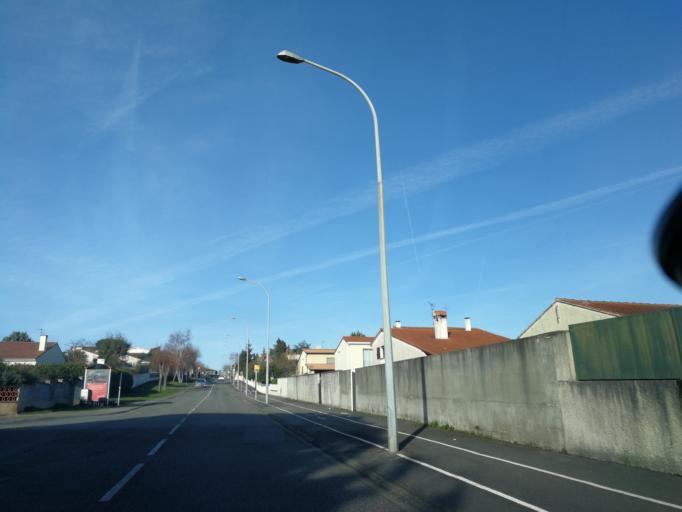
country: FR
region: Midi-Pyrenees
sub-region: Departement de la Haute-Garonne
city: Saint-Jean
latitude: 43.6491
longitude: 1.4962
